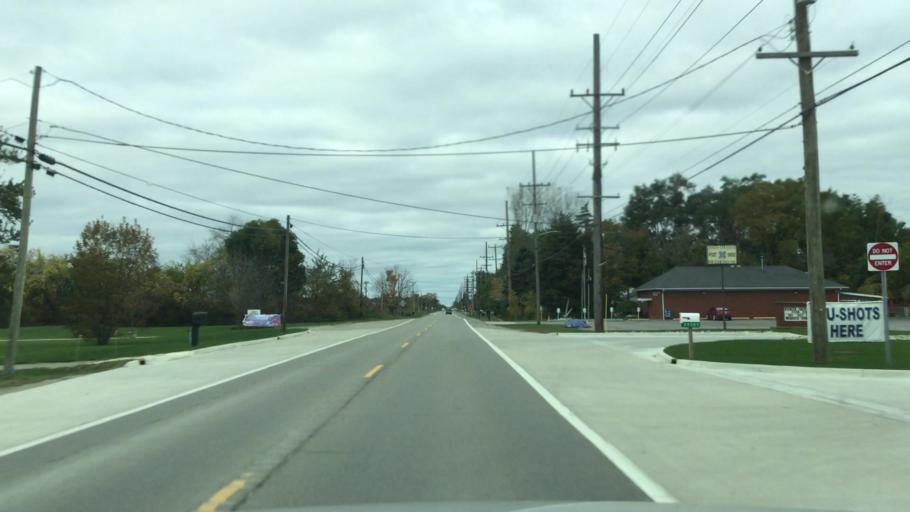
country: US
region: Michigan
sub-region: Macomb County
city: Richmond
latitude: 42.8089
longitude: -82.7695
